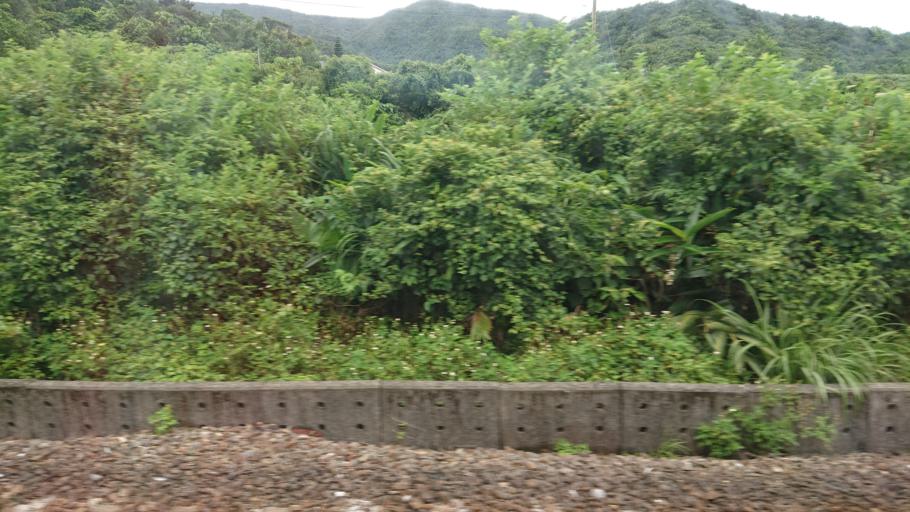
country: TW
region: Taiwan
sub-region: Keelung
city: Keelung
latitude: 25.0059
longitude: 121.9574
